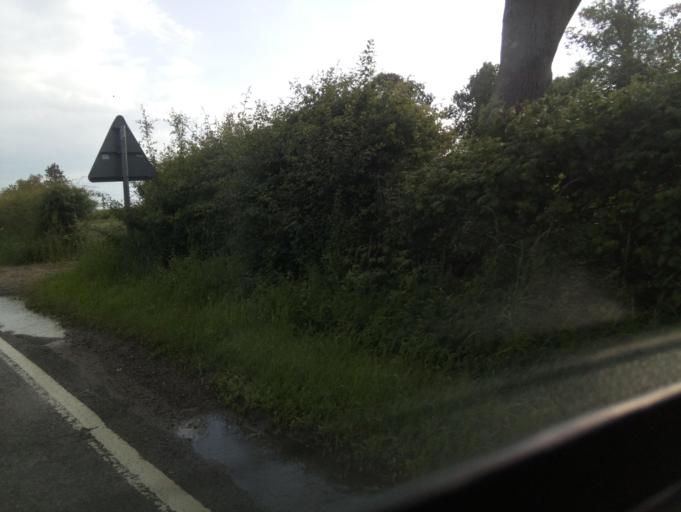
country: GB
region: England
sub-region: Lincolnshire
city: Great Gonerby
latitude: 52.9957
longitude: -0.6703
